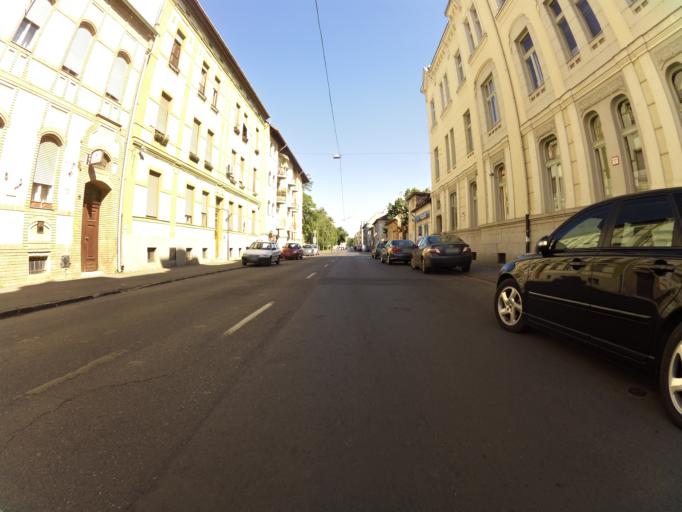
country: HU
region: Csongrad
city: Szeged
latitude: 46.2590
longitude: 20.1456
